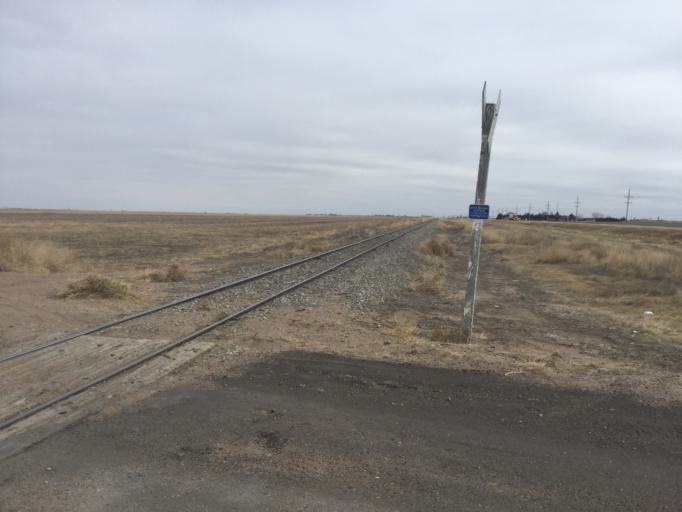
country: US
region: Kansas
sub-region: Haskell County
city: Sublette
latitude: 37.4915
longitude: -100.8165
